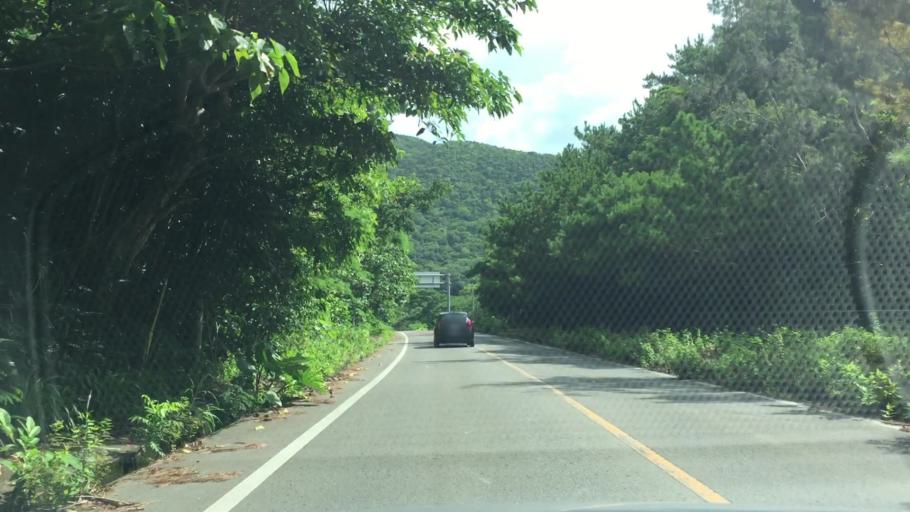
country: JP
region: Okinawa
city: Ishigaki
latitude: 24.4343
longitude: 124.2110
